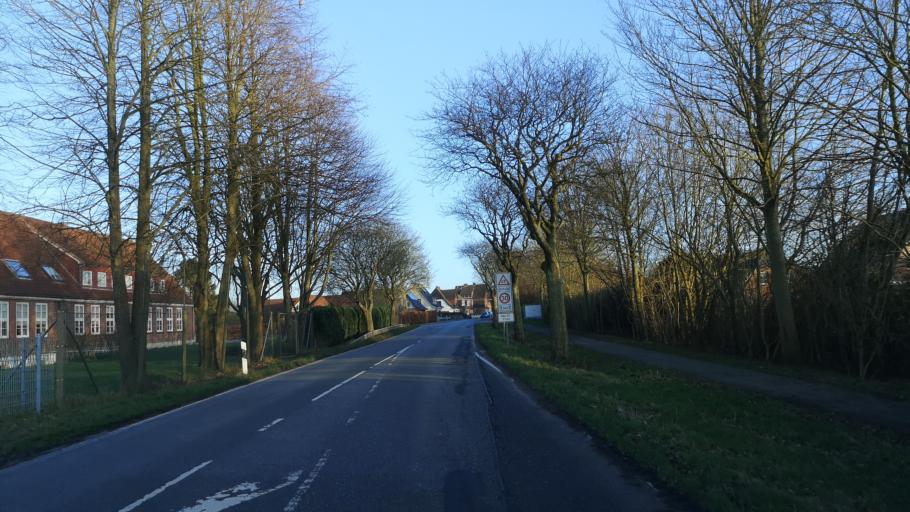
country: DE
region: Schleswig-Holstein
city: Satrup
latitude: 54.6948
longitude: 9.5888
